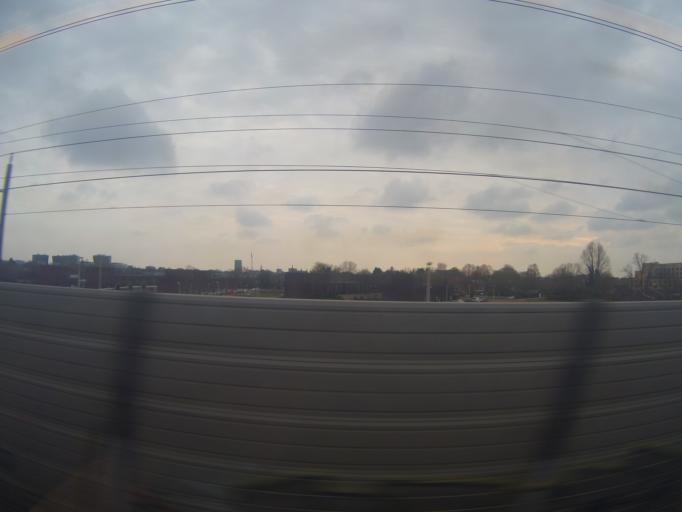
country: NL
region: Utrecht
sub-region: Stichtse Vecht
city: Maarssen
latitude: 52.1000
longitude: 5.0475
